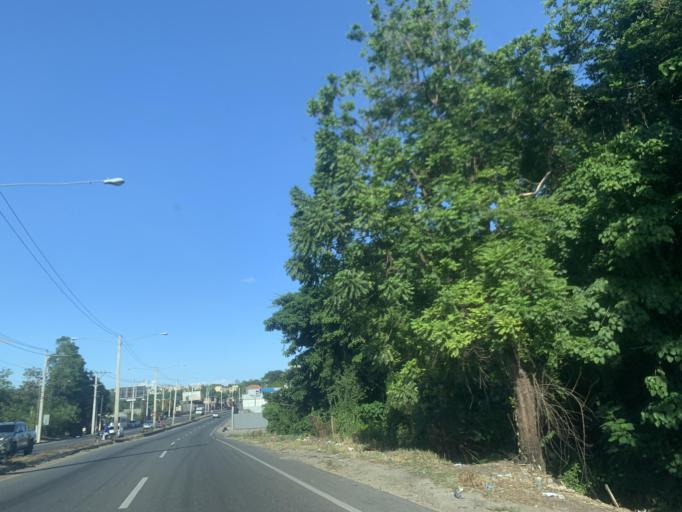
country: DO
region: San Cristobal
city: El Carril
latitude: 18.4357
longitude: -70.0169
